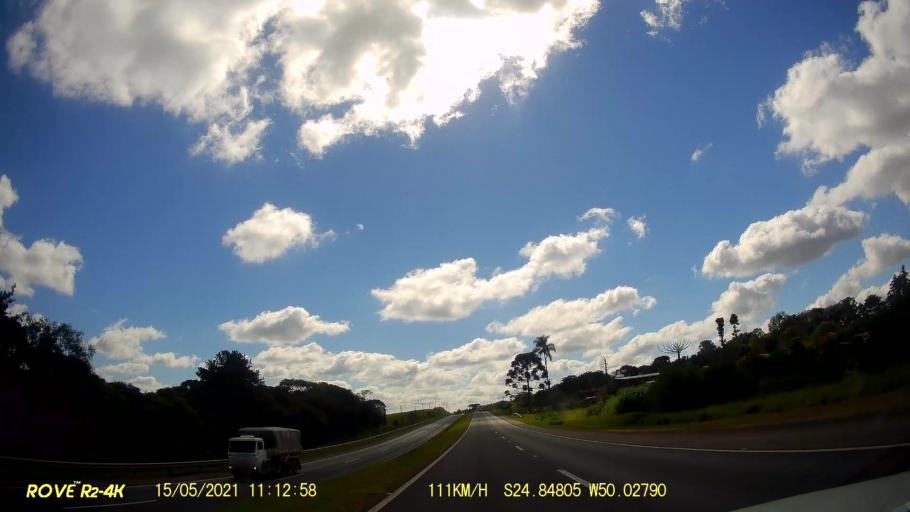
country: BR
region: Parana
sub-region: Castro
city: Castro
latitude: -24.8482
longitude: -50.0280
